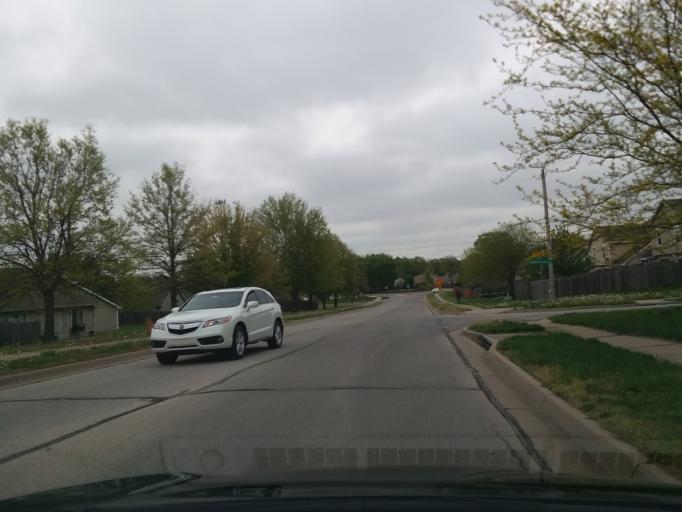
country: US
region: Kansas
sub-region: Douglas County
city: Lawrence
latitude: 38.9932
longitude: -95.2814
